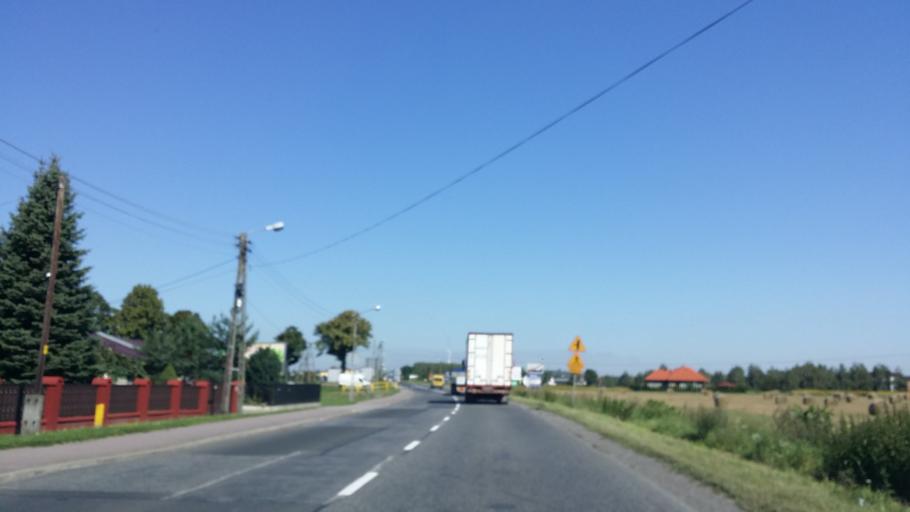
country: PL
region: Silesian Voivodeship
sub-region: Powiat bierunsko-ledzinski
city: Chelm Slaski
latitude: 50.1157
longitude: 19.2007
